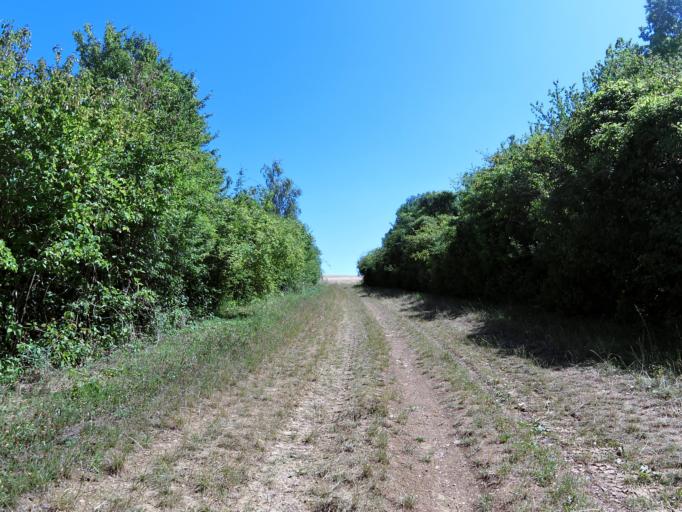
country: DE
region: Bavaria
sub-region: Regierungsbezirk Unterfranken
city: Gerbrunn
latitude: 49.7706
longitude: 10.0038
